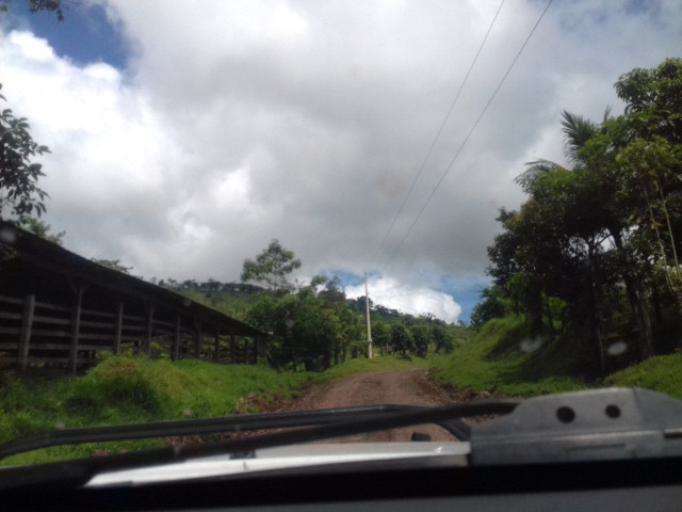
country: NI
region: Matagalpa
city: Rio Blanco
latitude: 12.9906
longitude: -85.1905
